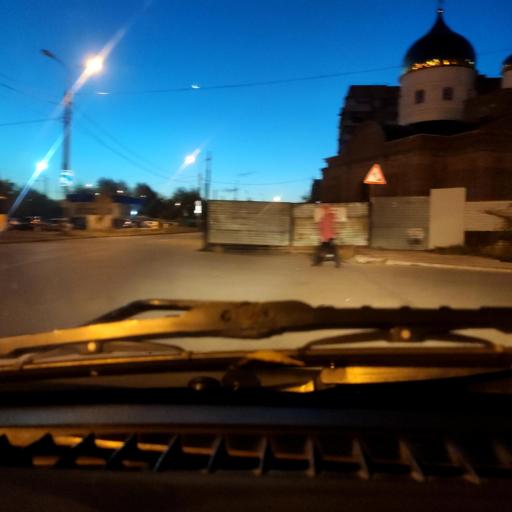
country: RU
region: Samara
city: Zhigulevsk
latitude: 53.4766
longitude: 49.5231
